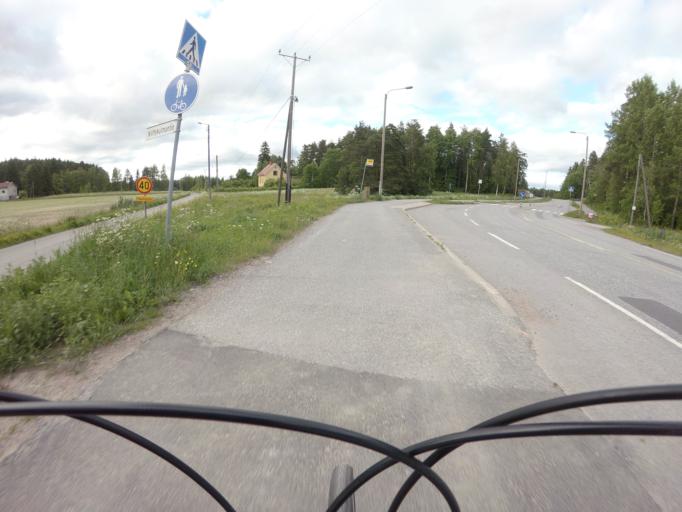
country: FI
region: Varsinais-Suomi
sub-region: Turku
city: Vahto
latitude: 60.5154
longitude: 22.3450
